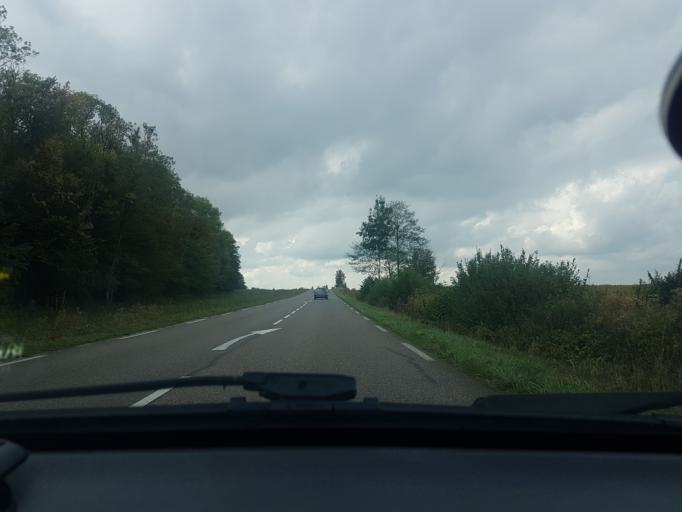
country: FR
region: Franche-Comte
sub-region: Departement de la Haute-Saone
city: Villersexel
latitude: 47.5432
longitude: 6.4989
